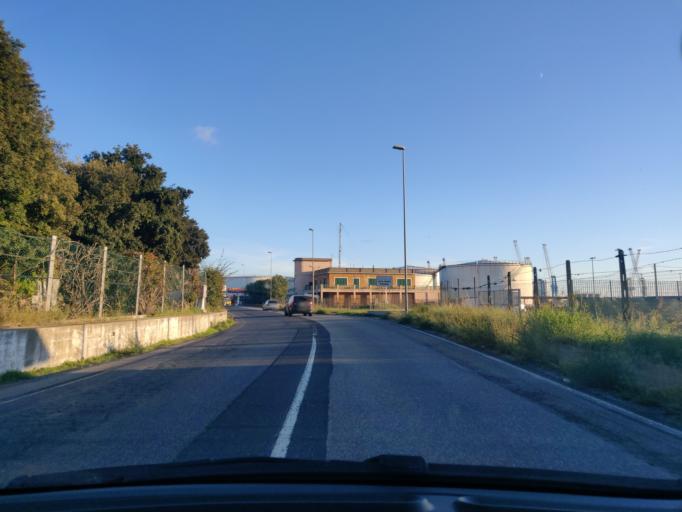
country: IT
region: Latium
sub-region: Citta metropolitana di Roma Capitale
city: Civitavecchia
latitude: 42.1096
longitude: 11.7778
